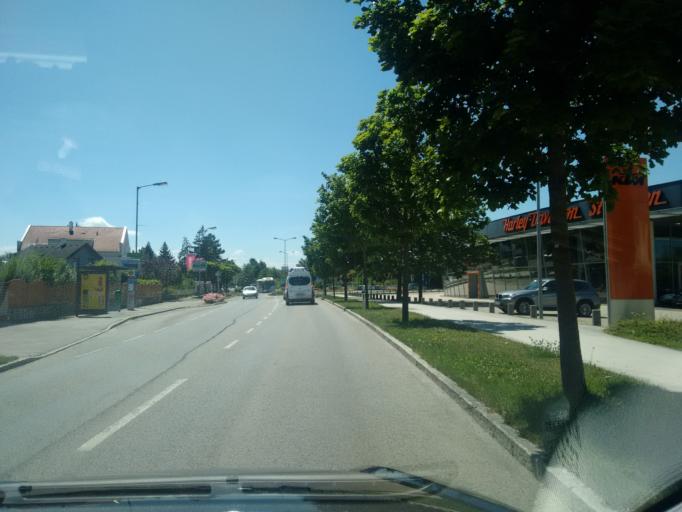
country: AT
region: Lower Austria
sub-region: Sankt Polten Stadt
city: Sankt Poelten
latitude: 48.2155
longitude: 15.6526
